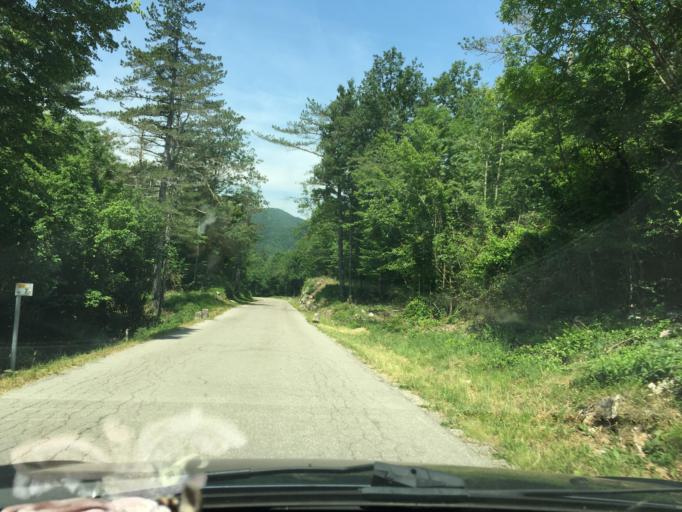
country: HR
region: Istarska
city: Buzet
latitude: 45.4601
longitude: 14.1367
